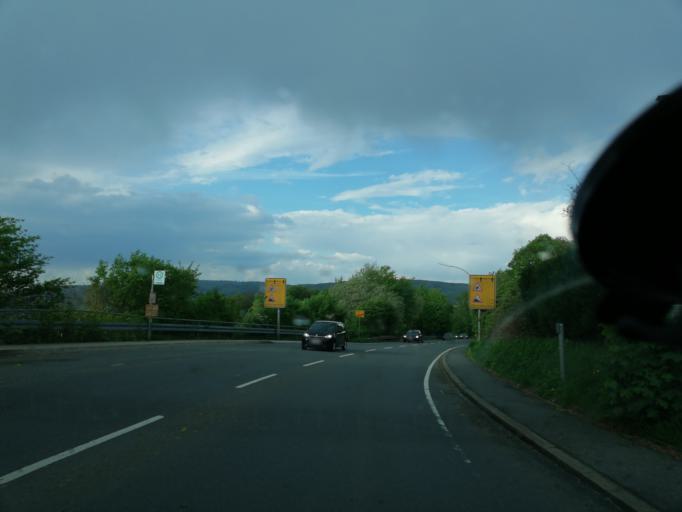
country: DE
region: North Rhine-Westphalia
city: Wetter (Ruhr)
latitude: 51.3790
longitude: 7.3735
